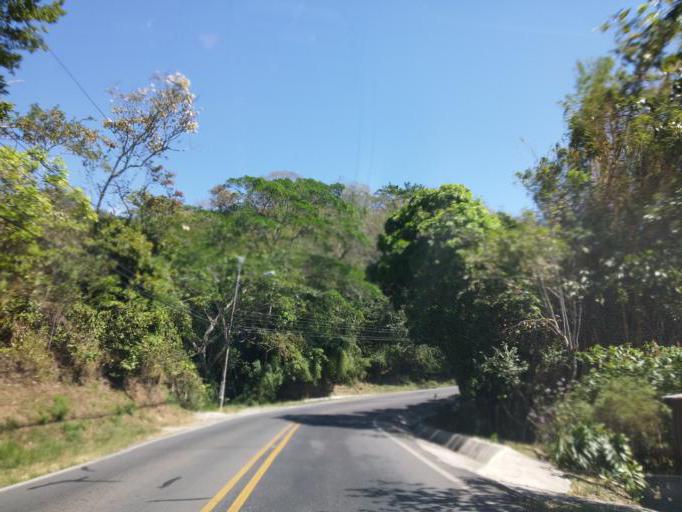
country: CR
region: Heredia
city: Colon
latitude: 9.8936
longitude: -84.2297
